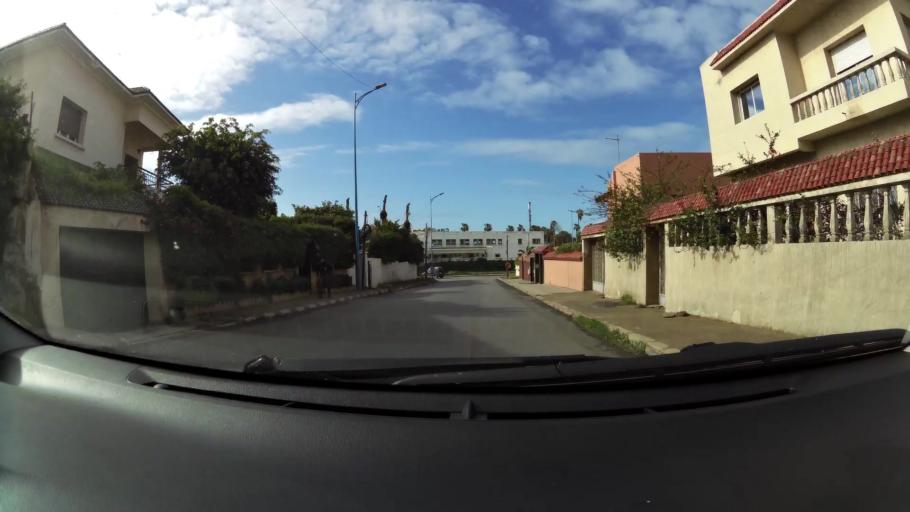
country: MA
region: Grand Casablanca
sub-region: Mohammedia
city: Mohammedia
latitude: 33.6947
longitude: -7.3869
